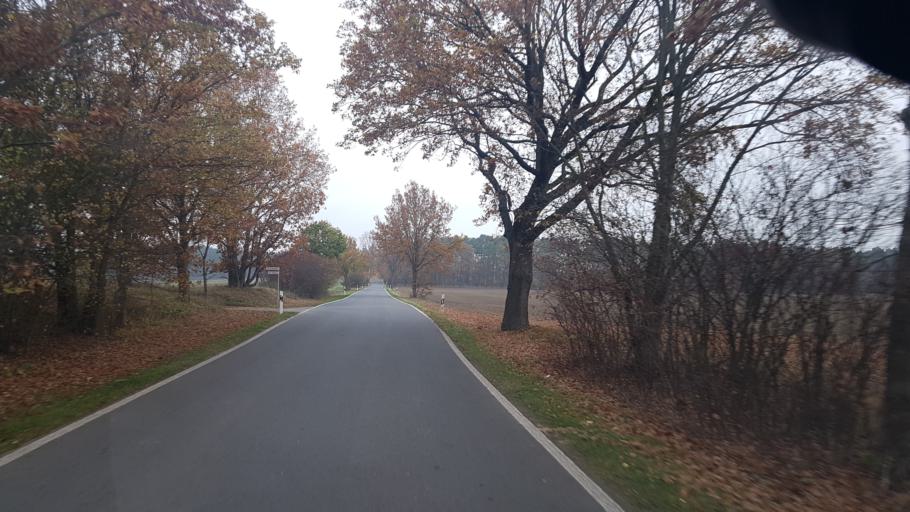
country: DE
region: Brandenburg
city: Lindow
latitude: 52.9530
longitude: 13.0073
